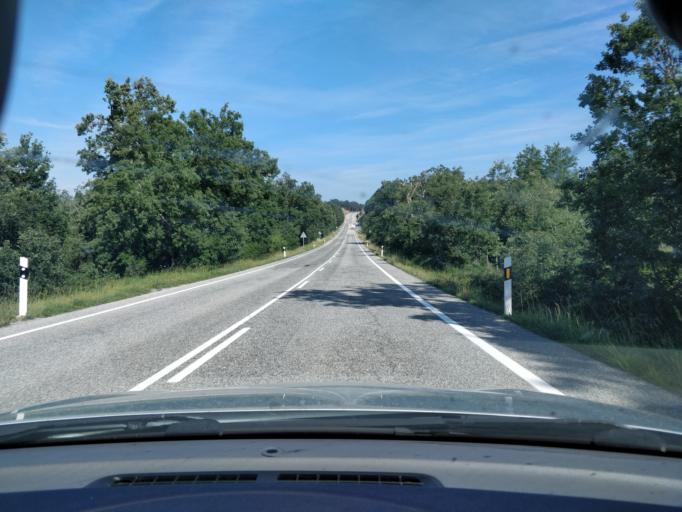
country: ES
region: Cantabria
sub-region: Provincia de Cantabria
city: San Martin de Elines
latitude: 42.9592
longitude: -3.7731
